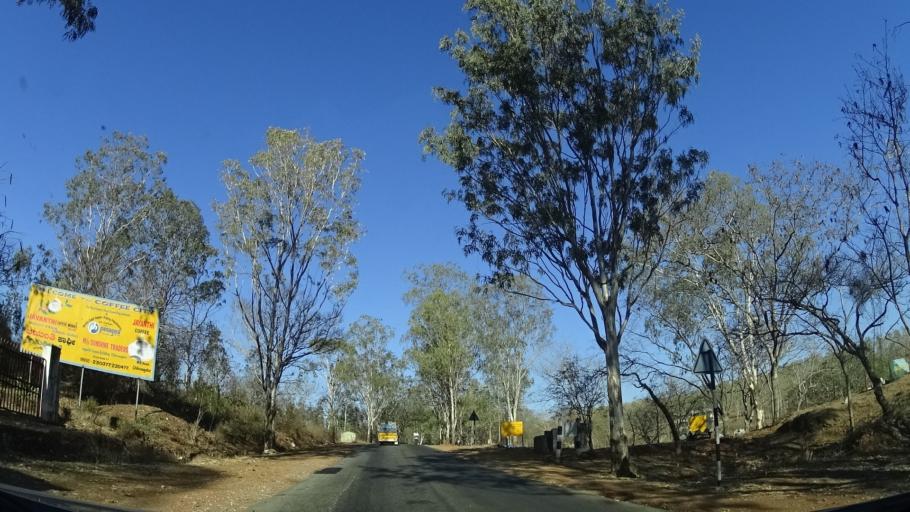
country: IN
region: Karnataka
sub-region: Chikmagalur
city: Chikmagalur
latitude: 13.3383
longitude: 75.8176
